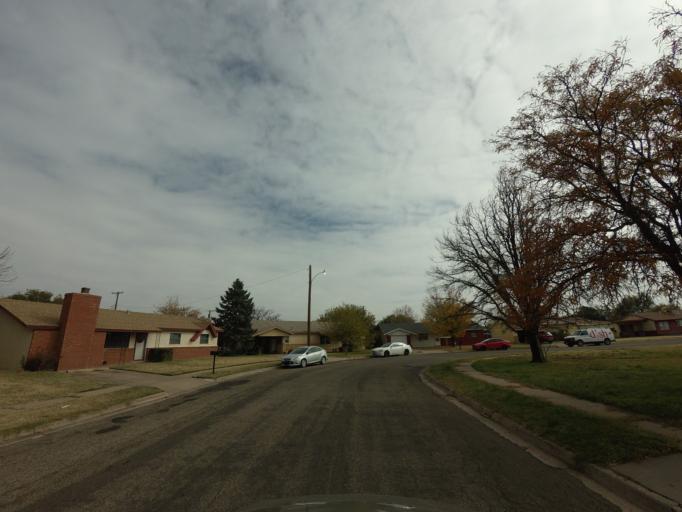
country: US
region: New Mexico
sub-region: Curry County
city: Clovis
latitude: 34.4291
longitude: -103.2219
